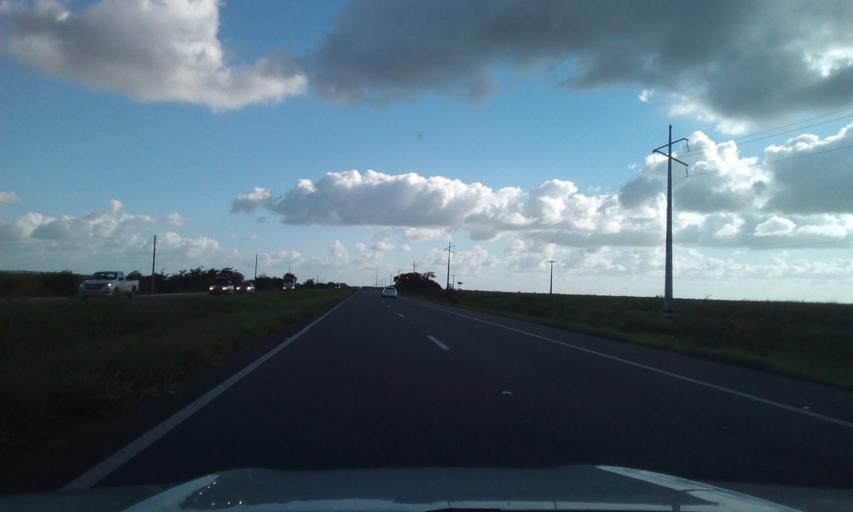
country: BR
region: Paraiba
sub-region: Cruz Do Espirito Santo
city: Cruz do Espirito Santo
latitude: -7.1848
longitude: -35.0547
